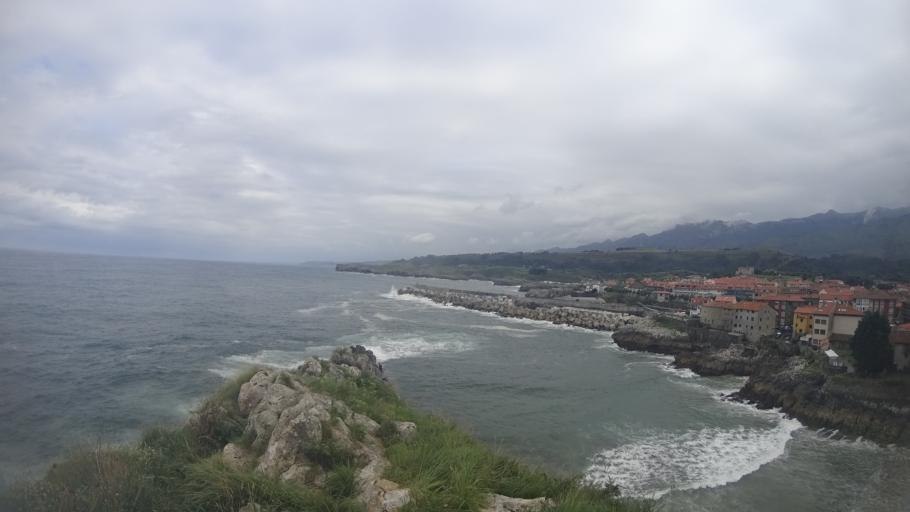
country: ES
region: Asturias
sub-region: Province of Asturias
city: Llanes
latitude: 43.4234
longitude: -4.7521
